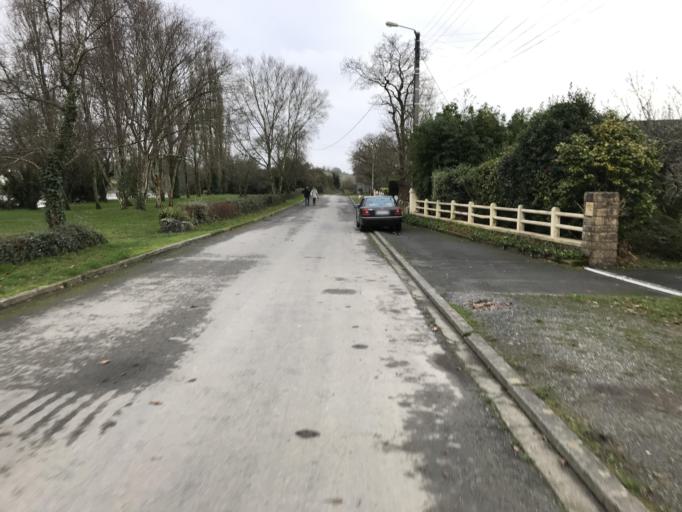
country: FR
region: Brittany
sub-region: Departement du Finistere
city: Daoulas
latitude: 48.3602
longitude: -4.2626
